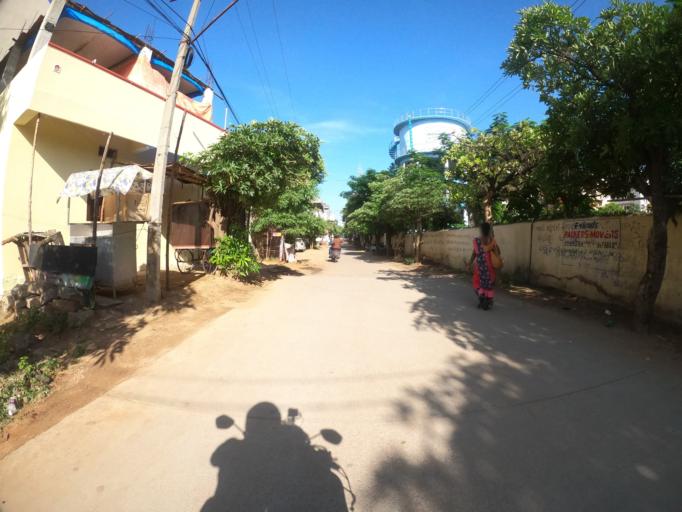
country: IN
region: Telangana
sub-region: Hyderabad
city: Hyderabad
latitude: 17.3520
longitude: 78.3771
